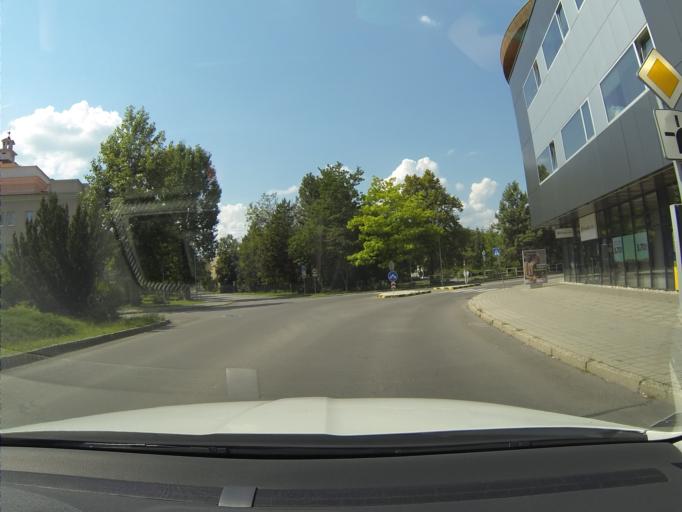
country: SK
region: Nitriansky
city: Prievidza
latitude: 48.7720
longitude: 18.6193
